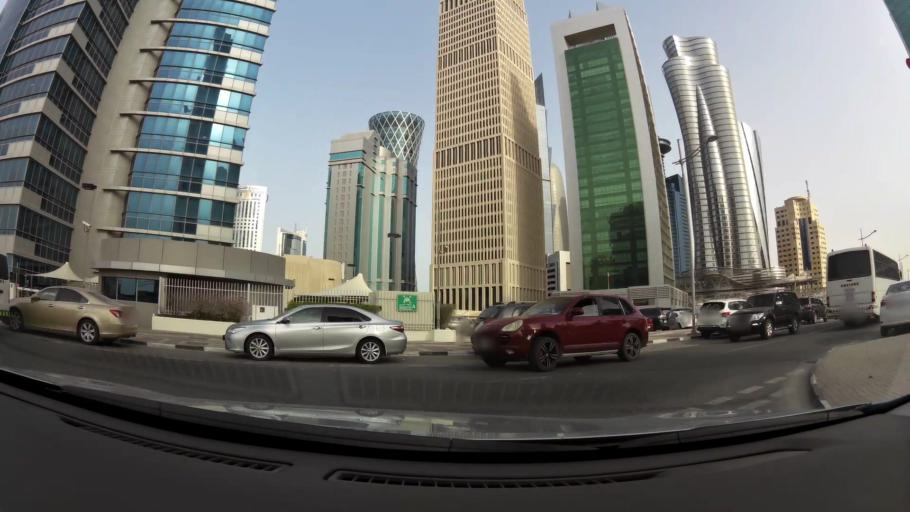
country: QA
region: Baladiyat ad Dawhah
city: Doha
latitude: 25.3202
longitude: 51.5240
